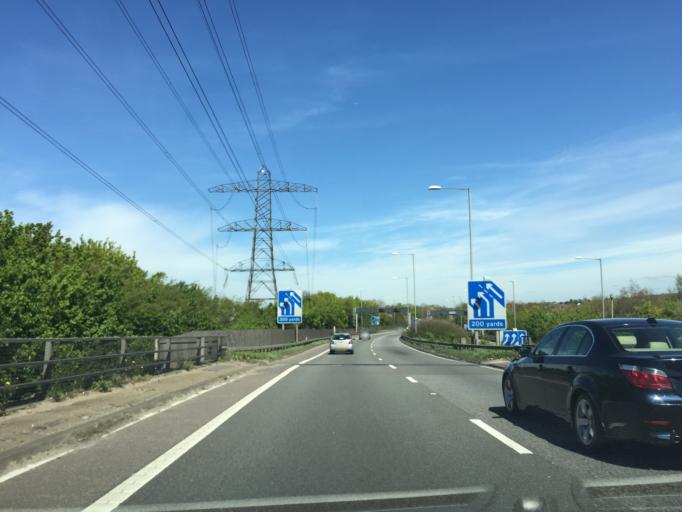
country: GB
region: England
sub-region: Greater London
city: Woodford Green
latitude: 51.5956
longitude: 0.0397
